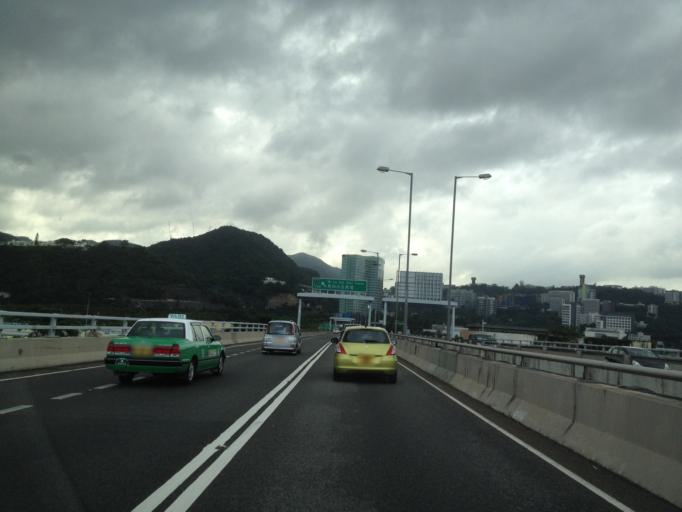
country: HK
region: Sha Tin
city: Sha Tin
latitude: 22.4066
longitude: 114.2172
